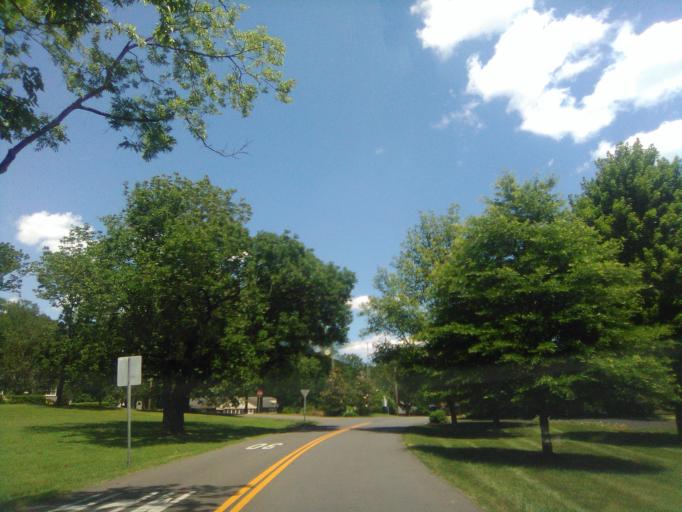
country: US
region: Tennessee
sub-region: Davidson County
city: Belle Meade
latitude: 36.1276
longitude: -86.8632
